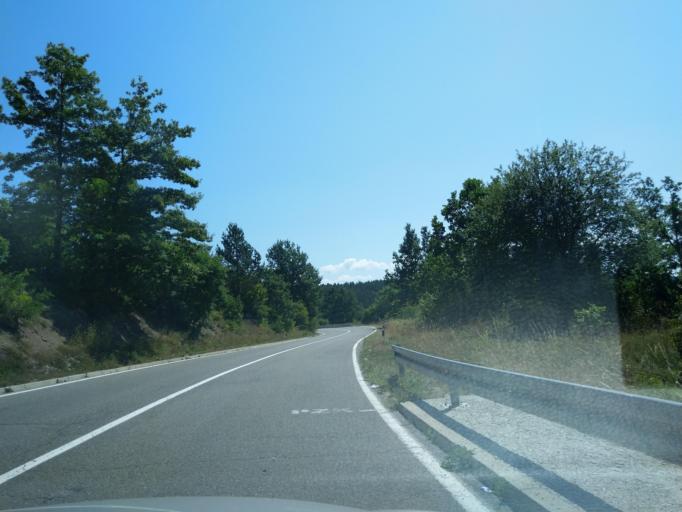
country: RS
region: Central Serbia
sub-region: Zlatiborski Okrug
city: Sjenica
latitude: 43.3065
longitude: 19.9241
